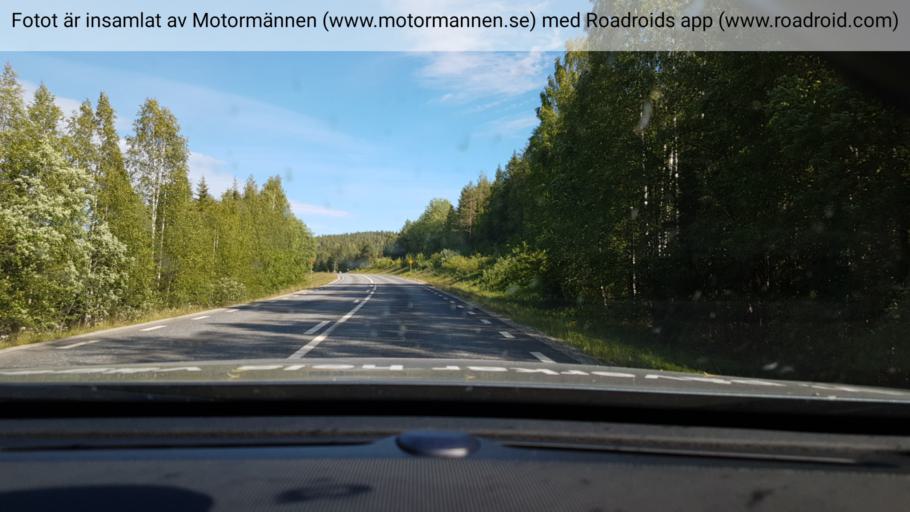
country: SE
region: Vaesterbotten
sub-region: Lycksele Kommun
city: Soderfors
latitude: 64.7053
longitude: 18.3220
